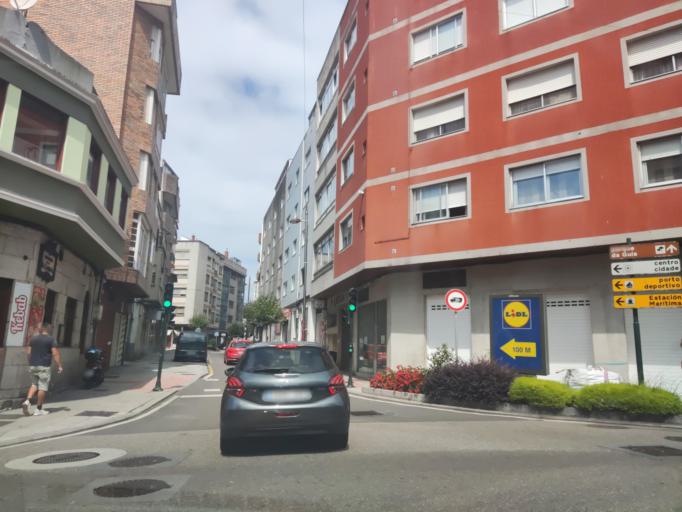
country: ES
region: Galicia
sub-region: Provincia de Pontevedra
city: Vigo
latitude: 42.2498
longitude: -8.6958
